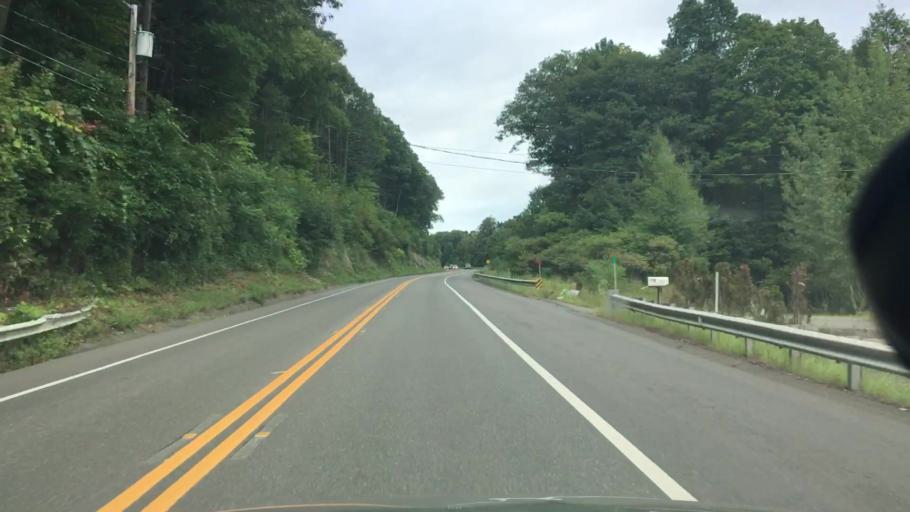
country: US
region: Massachusetts
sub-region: Franklin County
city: Greenfield
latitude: 42.5982
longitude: -72.6356
